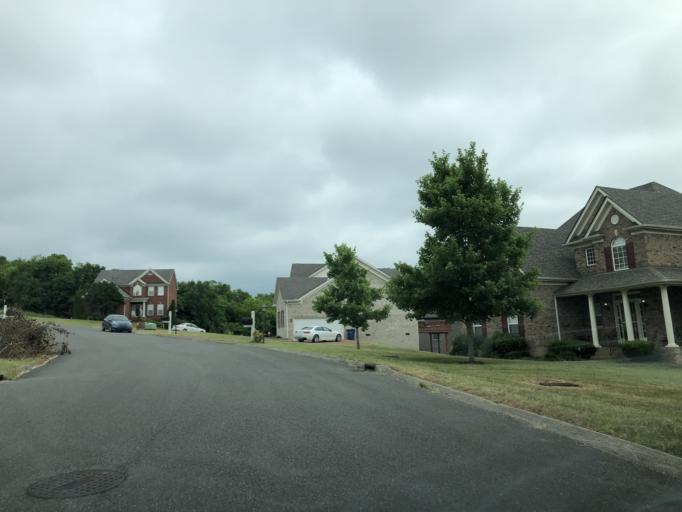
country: US
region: Tennessee
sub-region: Davidson County
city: Goodlettsville
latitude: 36.2936
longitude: -86.7350
